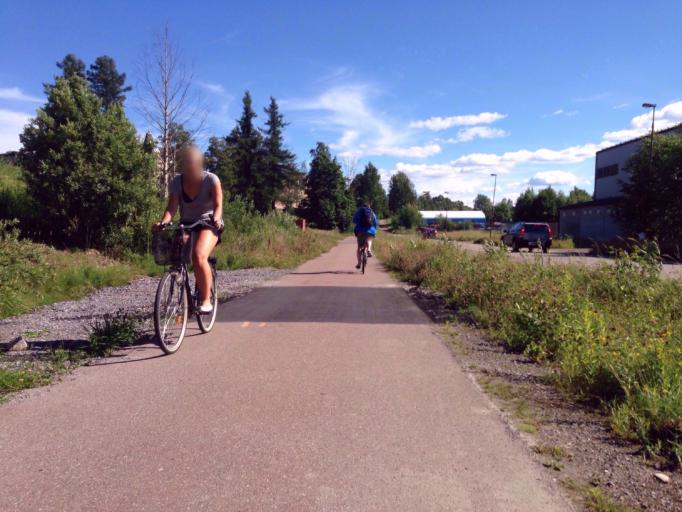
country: SE
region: Dalarna
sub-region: Ludvika Kommun
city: Ludvika
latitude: 60.1371
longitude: 15.1741
